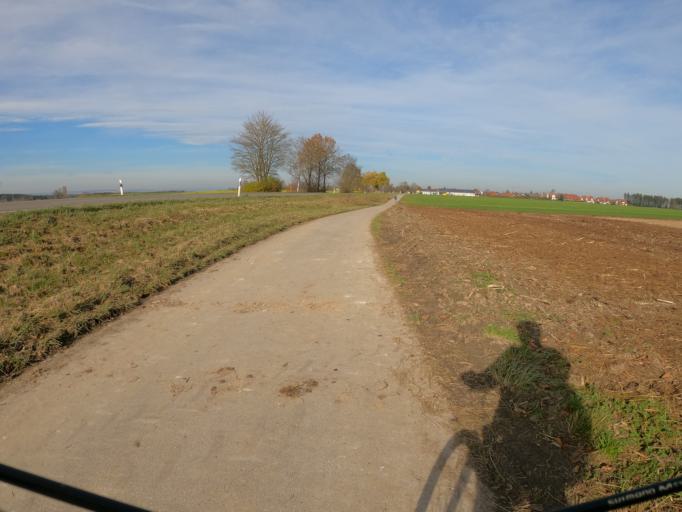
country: DE
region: Bavaria
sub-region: Swabia
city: Leipheim
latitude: 48.4089
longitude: 10.1953
